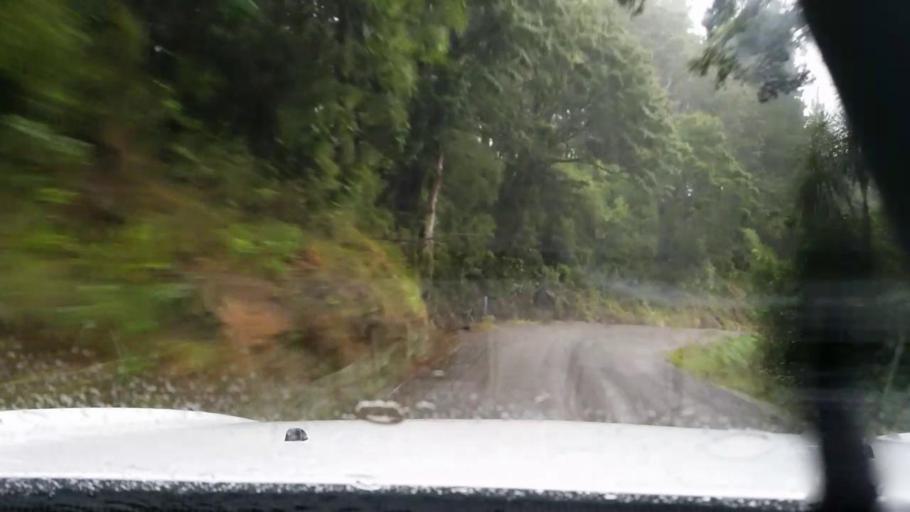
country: NZ
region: Wellington
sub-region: Masterton District
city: Masterton
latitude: -41.1875
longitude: 175.8183
